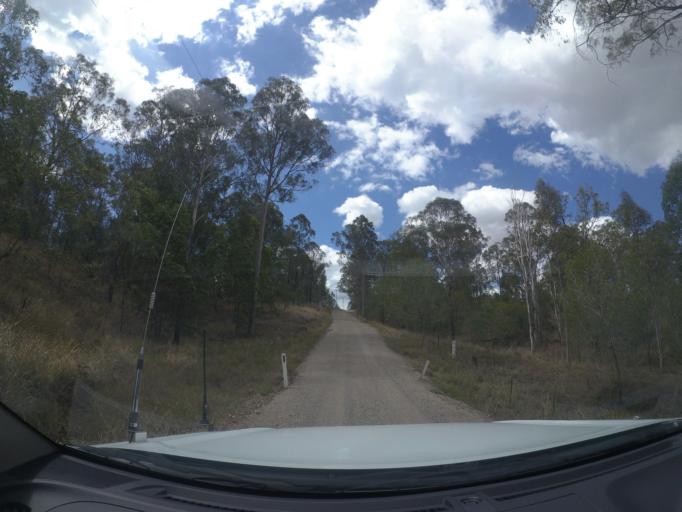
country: AU
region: Queensland
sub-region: Logan
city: Cedar Vale
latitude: -27.8992
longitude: 153.0007
